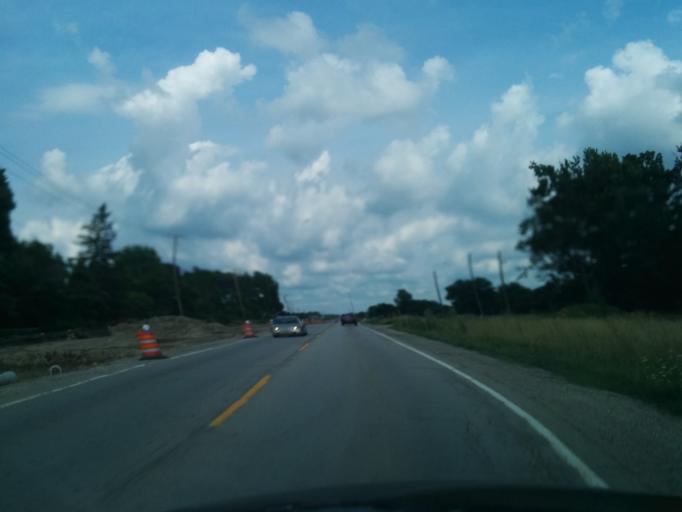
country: US
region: Illinois
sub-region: Will County
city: Homer Glen
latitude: 41.5992
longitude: -87.9620
